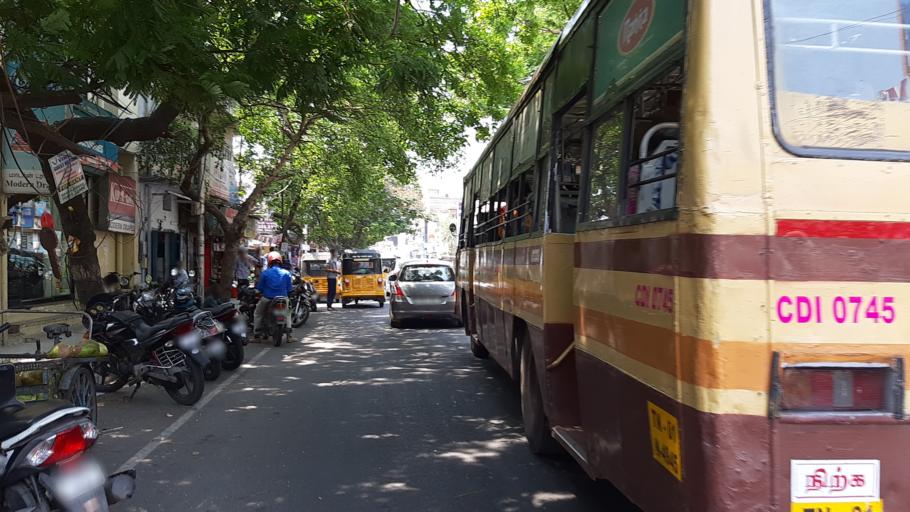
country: IN
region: Tamil Nadu
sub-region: Chennai
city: Chetput
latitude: 13.0600
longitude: 80.2426
